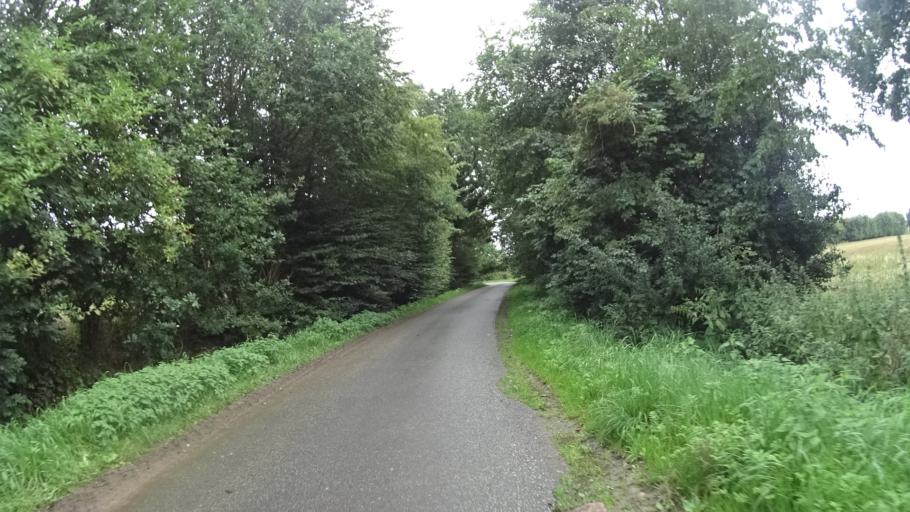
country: DE
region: Schleswig-Holstein
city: Stubben
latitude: 53.7135
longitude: 10.4464
